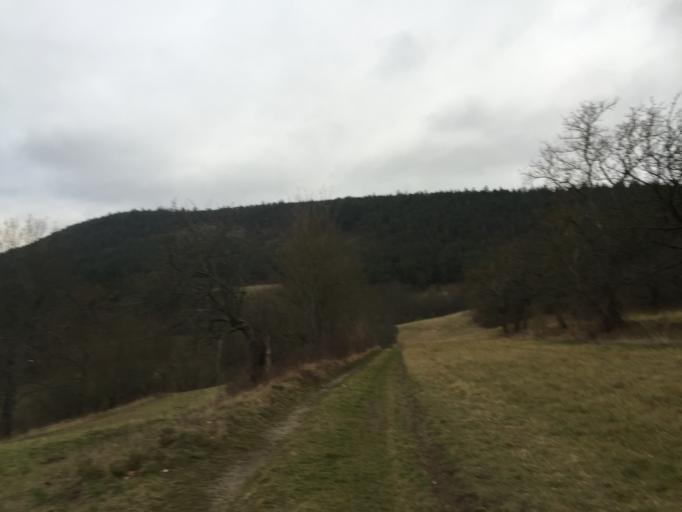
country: DE
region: Thuringia
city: Bad Blankenburg
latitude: 50.6998
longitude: 11.2526
